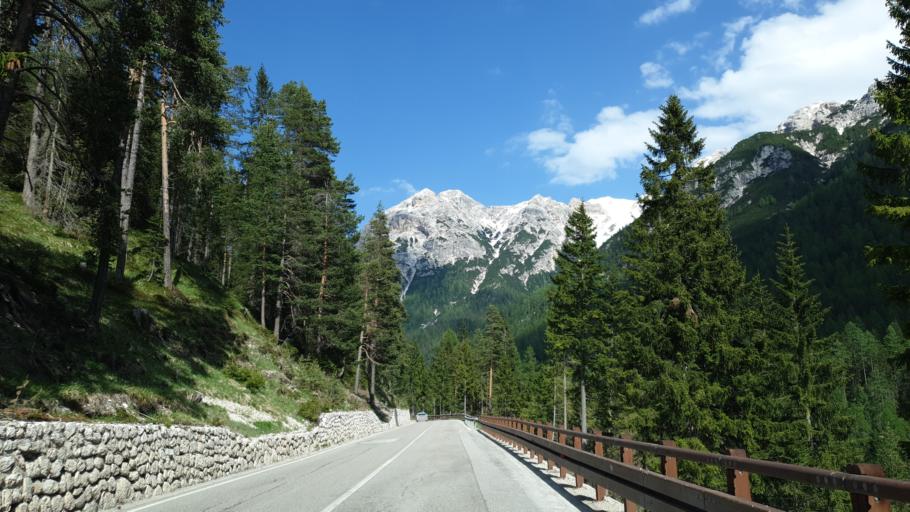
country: IT
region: Veneto
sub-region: Provincia di Belluno
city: Cortina d'Ampezzo
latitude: 46.6014
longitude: 12.1333
